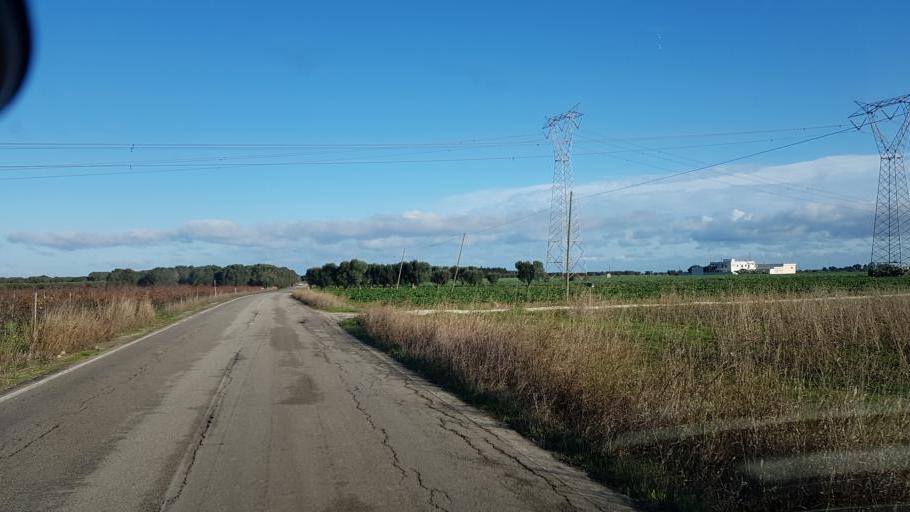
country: IT
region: Apulia
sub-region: Provincia di Brindisi
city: Tuturano
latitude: 40.5582
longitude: 17.9477
